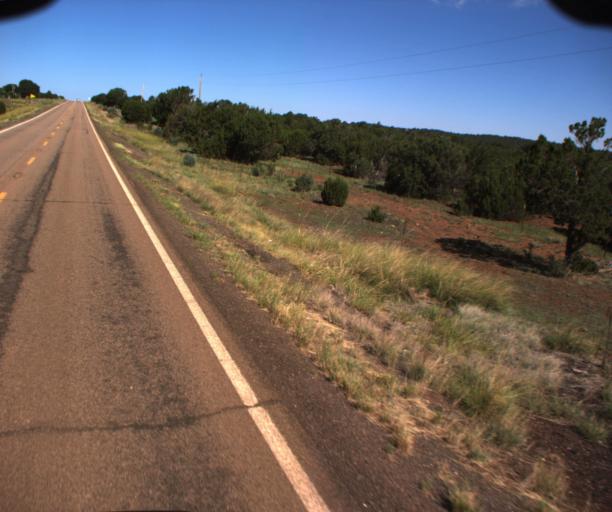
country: US
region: Arizona
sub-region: Navajo County
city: Pinetop-Lakeside
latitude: 34.2784
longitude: -109.7978
